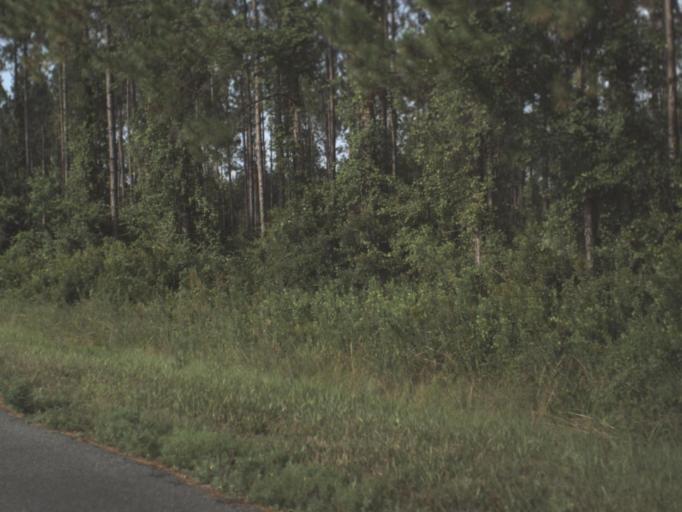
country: US
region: Florida
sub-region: Taylor County
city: Perry
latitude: 30.2293
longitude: -83.6169
